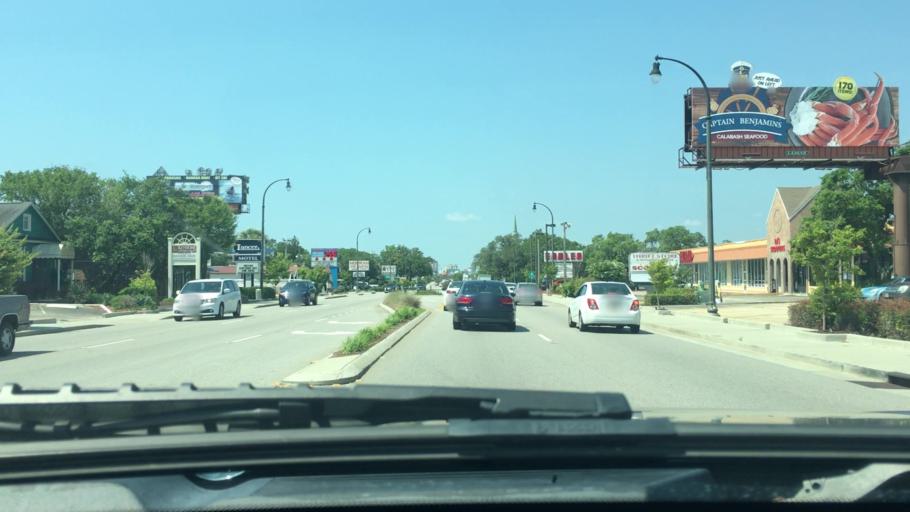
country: US
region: South Carolina
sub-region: Horry County
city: Myrtle Beach
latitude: 33.6919
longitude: -78.8848
